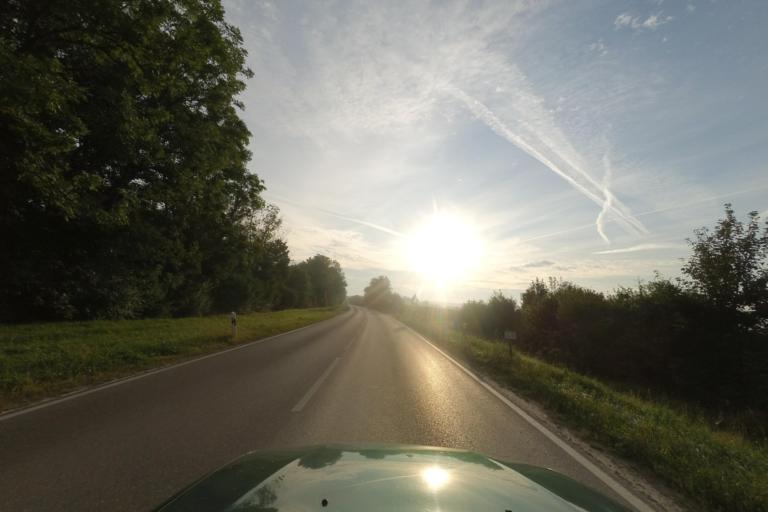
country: DE
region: Bavaria
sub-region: Upper Bavaria
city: Landsberied
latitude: 48.1681
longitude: 11.1577
